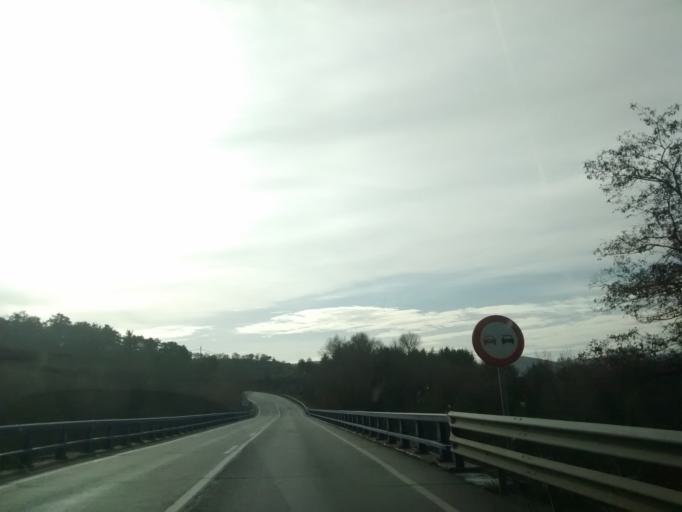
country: ES
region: Aragon
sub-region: Provincia de Zaragoza
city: Mianos
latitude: 42.6119
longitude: -0.9025
